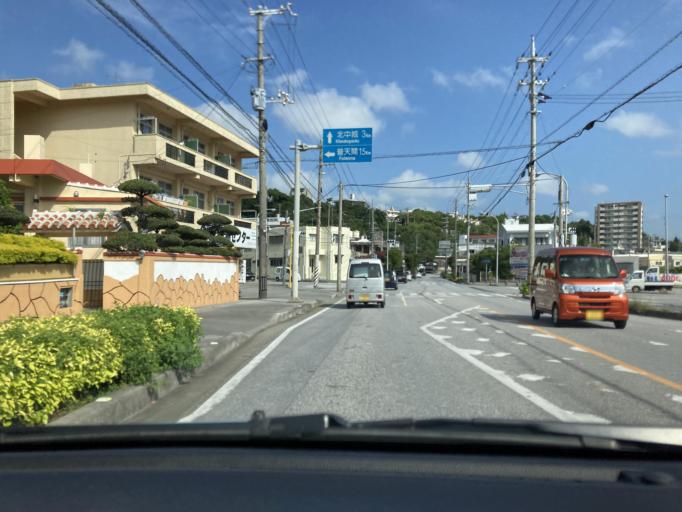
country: JP
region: Okinawa
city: Ginowan
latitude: 26.2824
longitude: 127.7848
